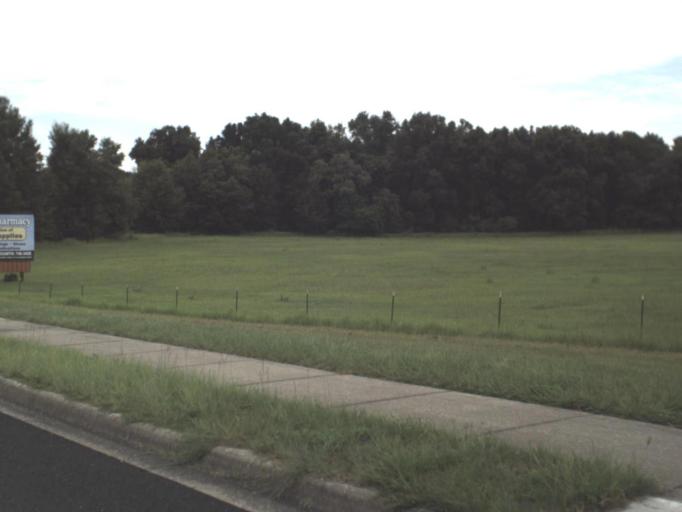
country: US
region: Florida
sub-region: Citrus County
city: Lecanto
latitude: 28.8535
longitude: -82.4980
